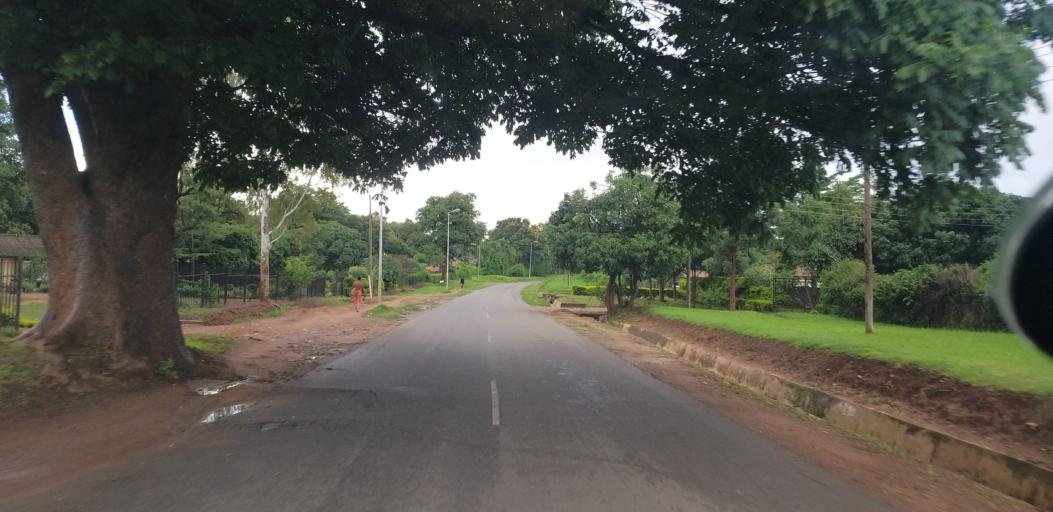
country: ZM
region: Lusaka
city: Lusaka
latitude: -15.4295
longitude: 28.3323
